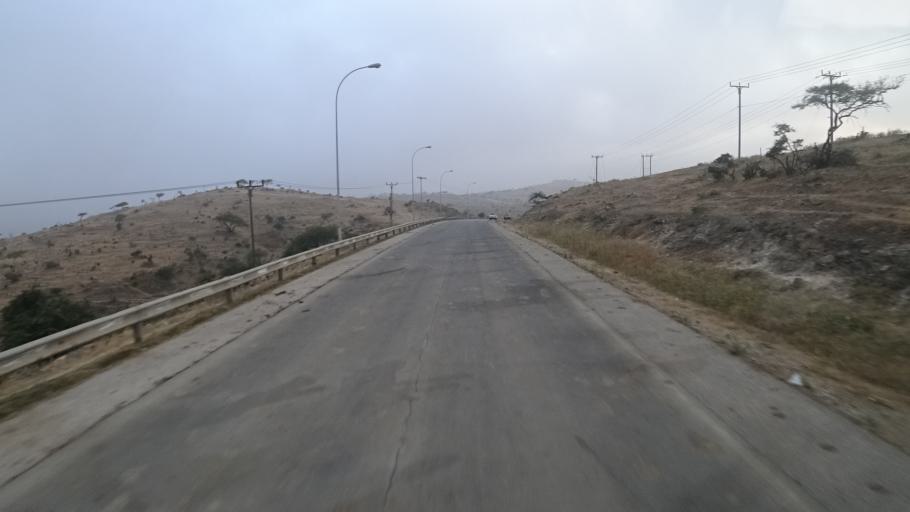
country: OM
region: Zufar
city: Salalah
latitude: 17.1314
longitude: 53.9622
